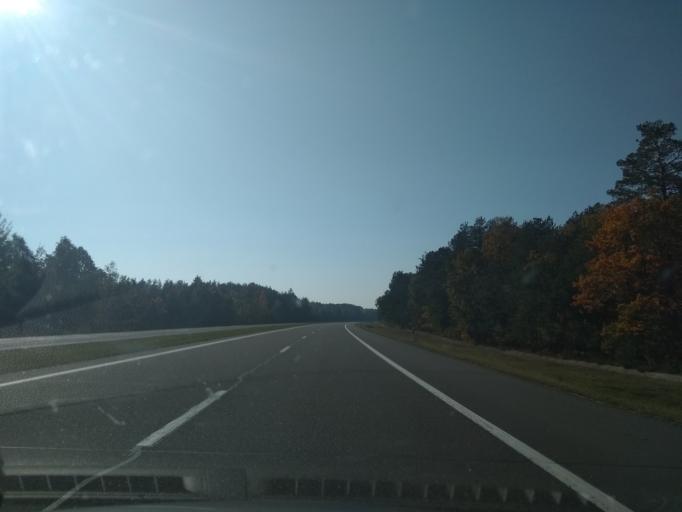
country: BY
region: Brest
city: Antopal'
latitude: 52.3691
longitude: 24.7401
